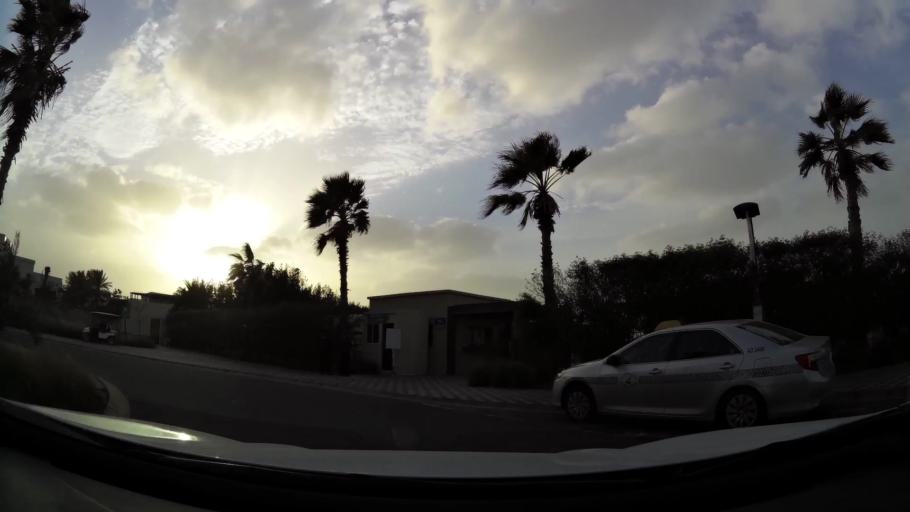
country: AE
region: Abu Dhabi
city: Abu Dhabi
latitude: 24.5470
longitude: 54.4360
